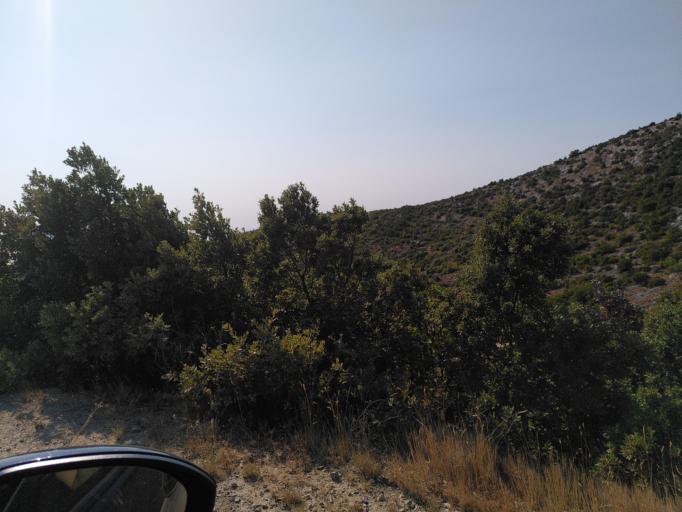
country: HR
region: Splitsko-Dalmatinska
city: Stari Grad
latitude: 43.1534
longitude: 16.5807
